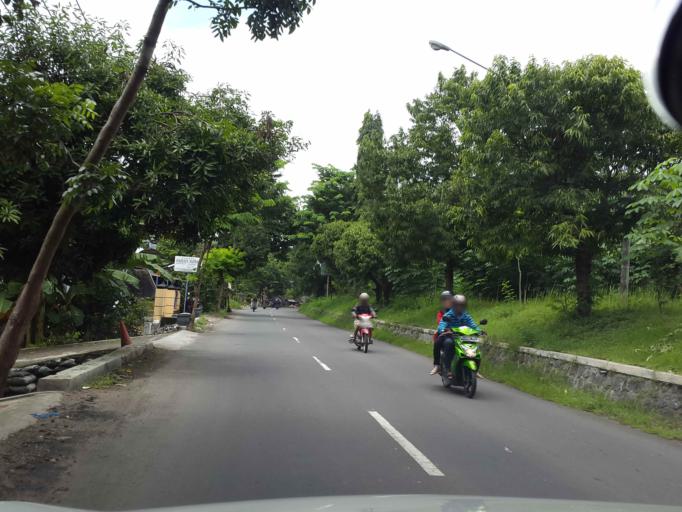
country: ID
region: East Java
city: Mojokerto
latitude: -7.4583
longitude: 112.4242
